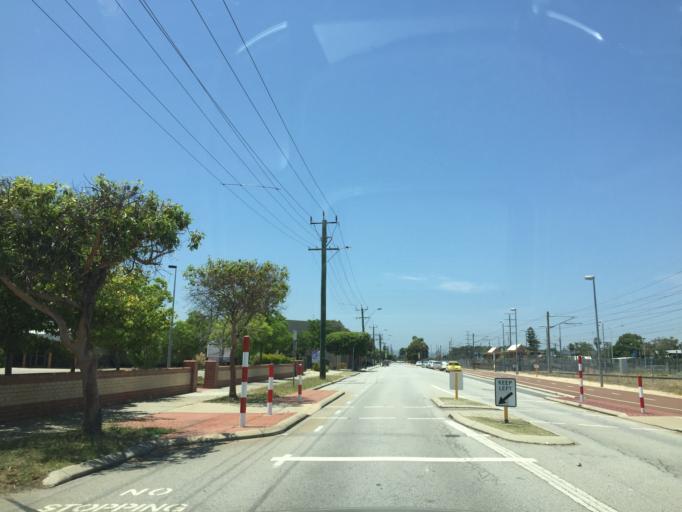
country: AU
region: Western Australia
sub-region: Canning
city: Queens Park
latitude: -32.0062
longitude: 115.9379
